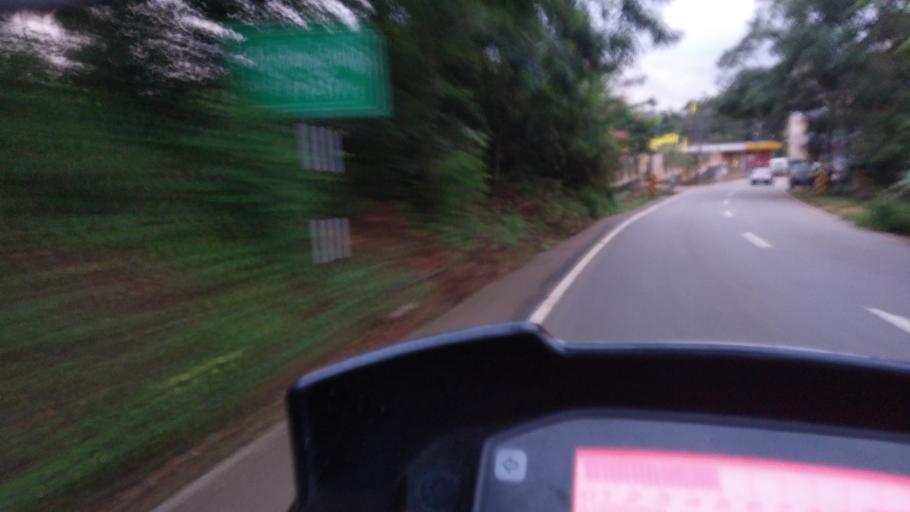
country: IN
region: Kerala
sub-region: Idukki
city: Munnar
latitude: 9.9687
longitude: 77.1156
